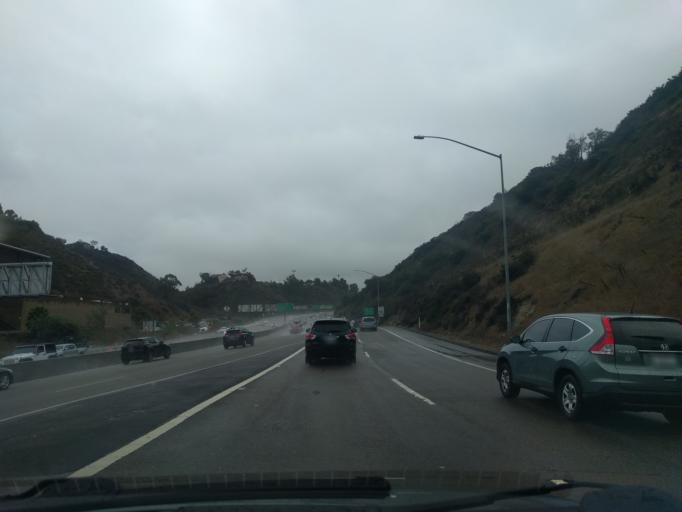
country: US
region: California
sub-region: San Diego County
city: San Diego
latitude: 32.7600
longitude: -117.1629
